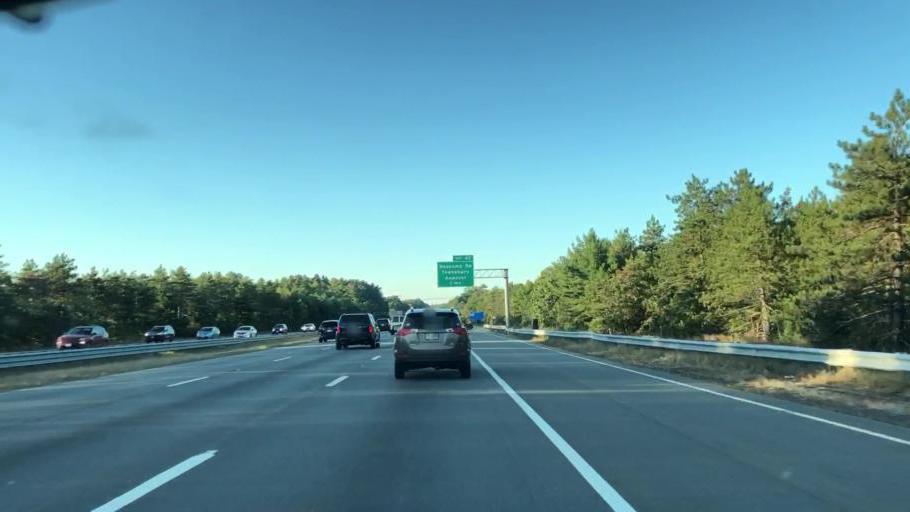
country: US
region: Massachusetts
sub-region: Middlesex County
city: Wilmington
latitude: 42.6078
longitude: -71.1724
